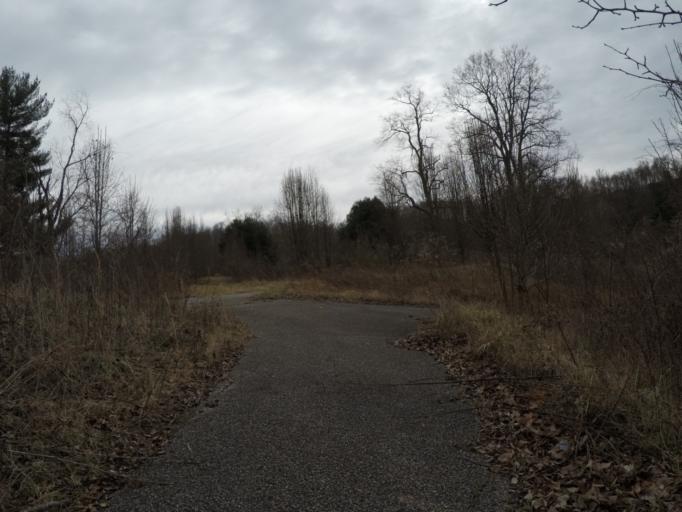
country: US
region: Ohio
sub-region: Lawrence County
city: Burlington
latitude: 38.3833
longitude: -82.5099
